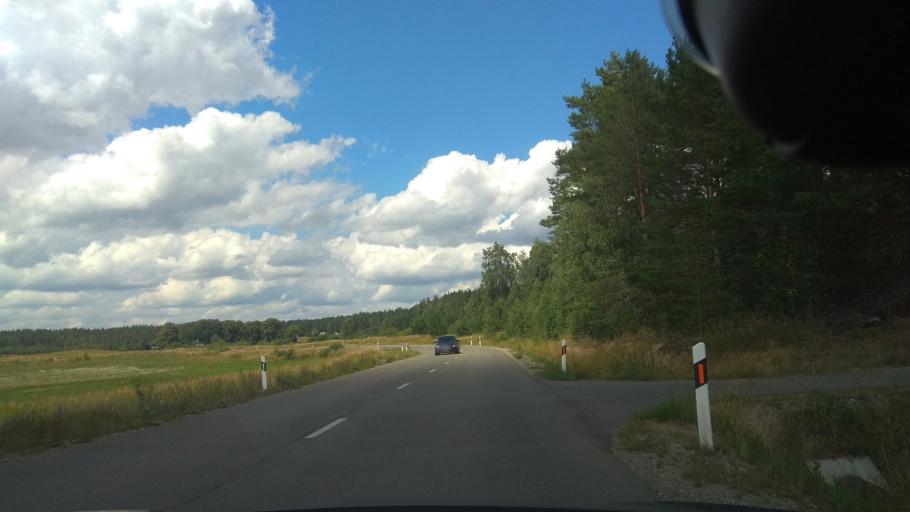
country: LT
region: Vilnius County
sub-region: Trakai
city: Rudiskes
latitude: 54.5099
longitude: 24.8639
